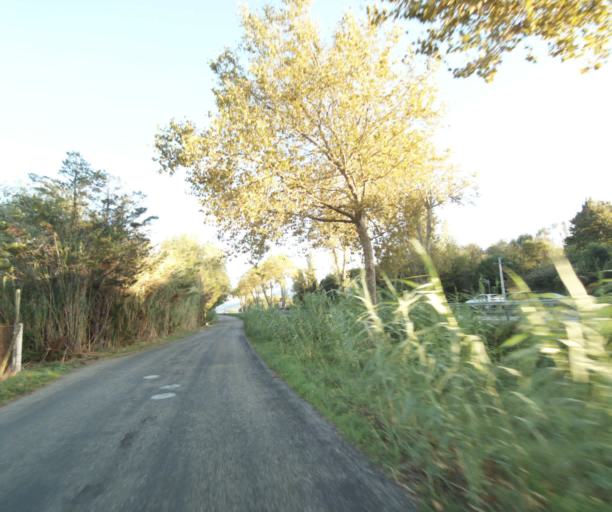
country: FR
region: Languedoc-Roussillon
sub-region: Departement des Pyrenees-Orientales
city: Elne
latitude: 42.5791
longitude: 2.9916
